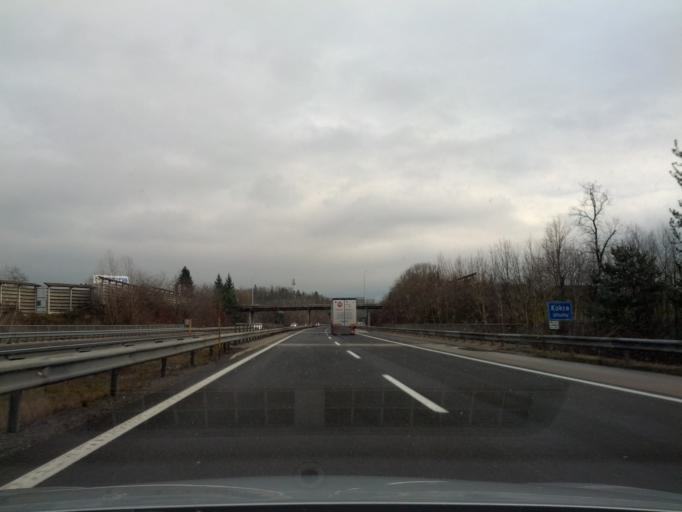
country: SI
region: Kranj
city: Britof
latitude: 46.2573
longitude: 14.3786
